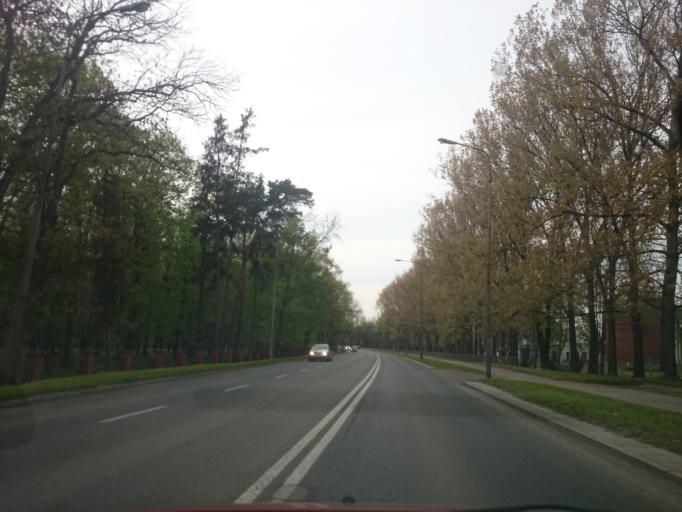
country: PL
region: Opole Voivodeship
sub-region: Powiat opolski
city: Opole
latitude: 50.6748
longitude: 17.9084
